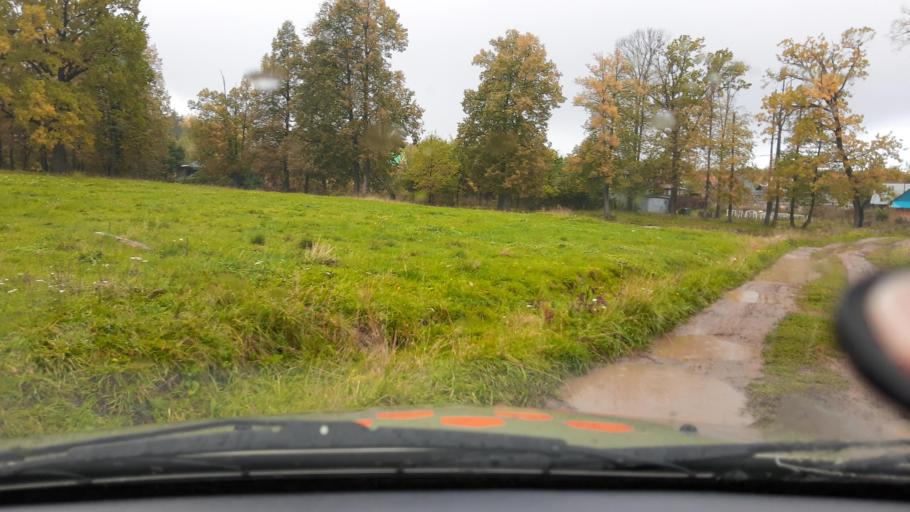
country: RU
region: Bashkortostan
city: Kudeyevskiy
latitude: 54.8746
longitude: 56.6273
